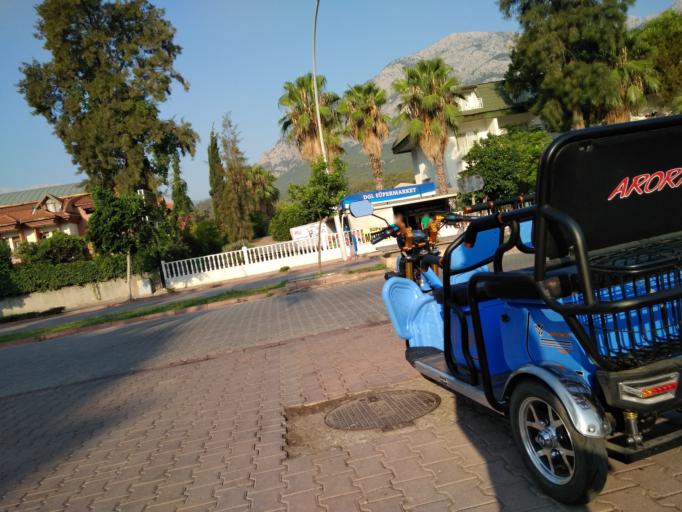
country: TR
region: Antalya
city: Kemer
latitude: 36.6163
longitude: 30.5556
